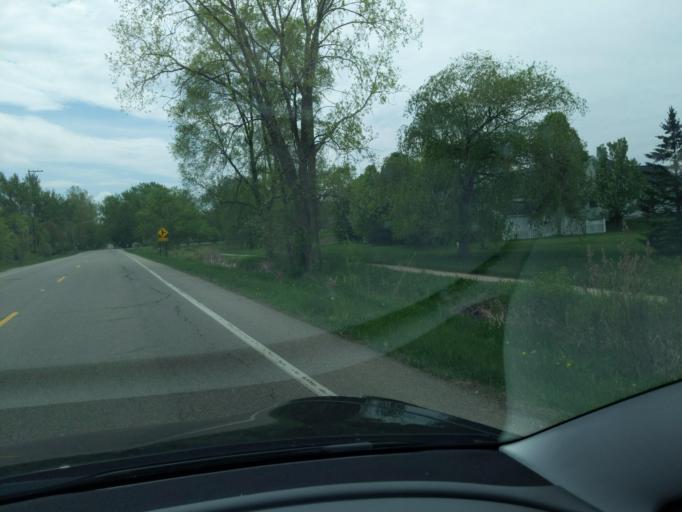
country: US
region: Michigan
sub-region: Ingham County
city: Holt
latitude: 42.6274
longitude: -84.5429
